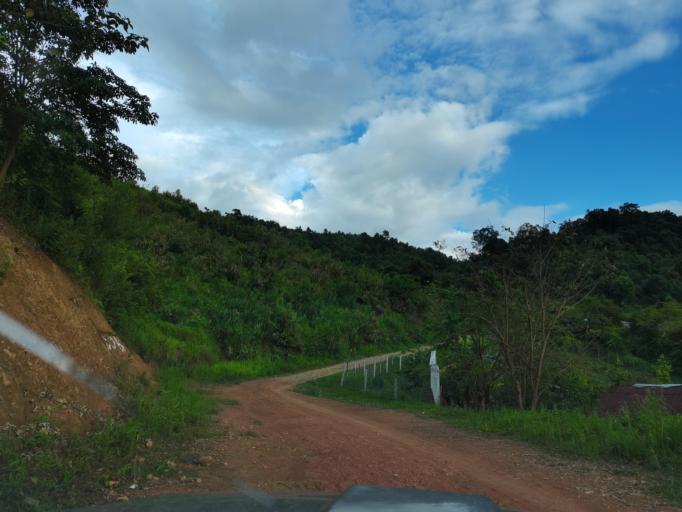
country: LA
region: Phongsali
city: Phongsali
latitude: 21.6760
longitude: 102.1883
